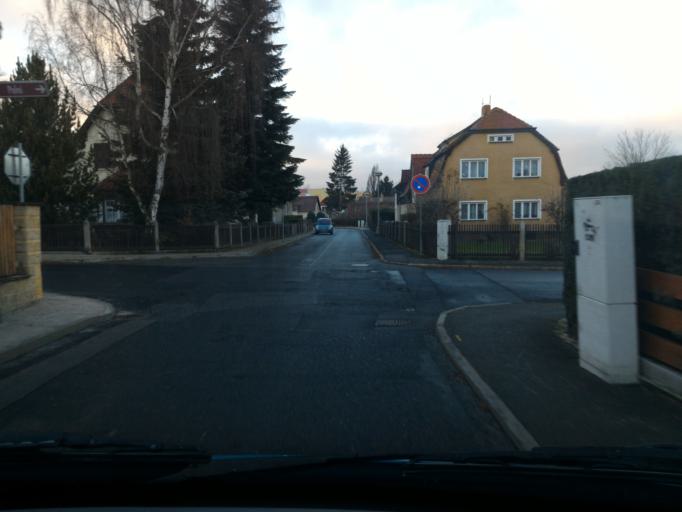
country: CZ
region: Ustecky
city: Varnsdorf
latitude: 50.9037
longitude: 14.6224
